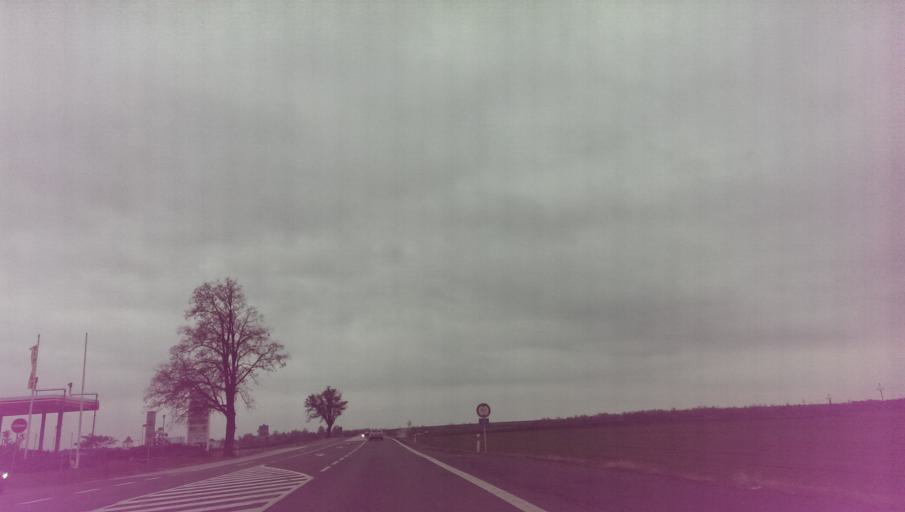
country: CZ
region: South Moravian
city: Miroslav
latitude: 48.9288
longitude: 16.3532
